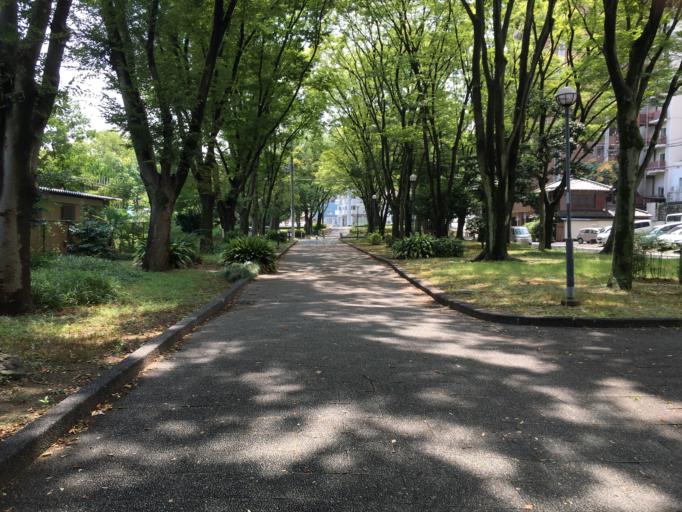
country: JP
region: Aichi
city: Nagoya-shi
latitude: 35.1485
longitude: 136.9043
